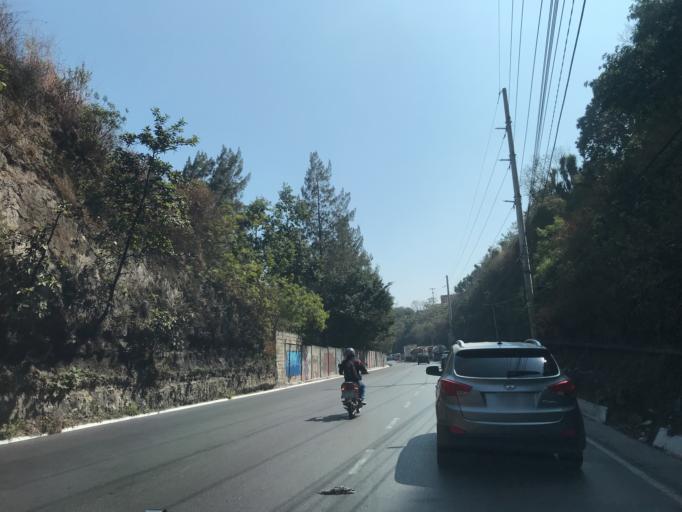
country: GT
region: Guatemala
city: Petapa
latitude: 14.5248
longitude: -90.5576
